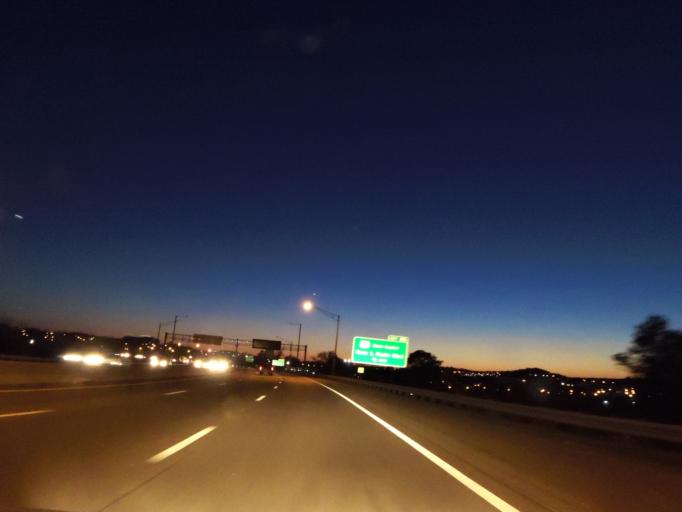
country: US
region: Tennessee
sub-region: Davidson County
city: Nashville
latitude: 36.1918
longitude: -86.7856
